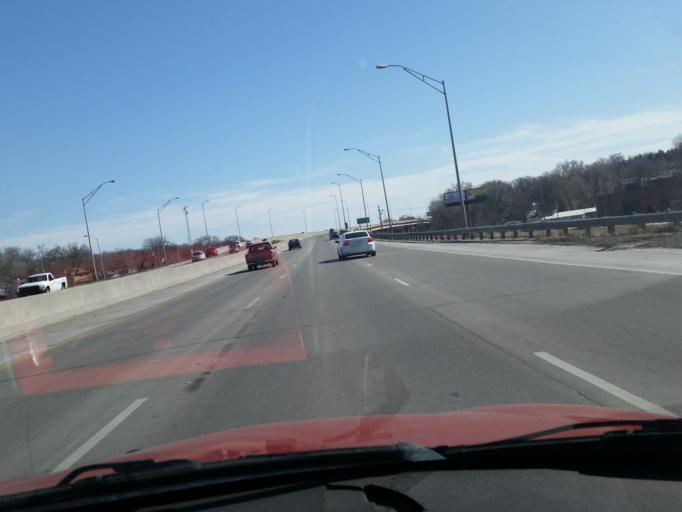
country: US
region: Nebraska
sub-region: Douglas County
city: Omaha
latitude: 41.1983
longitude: -95.9445
